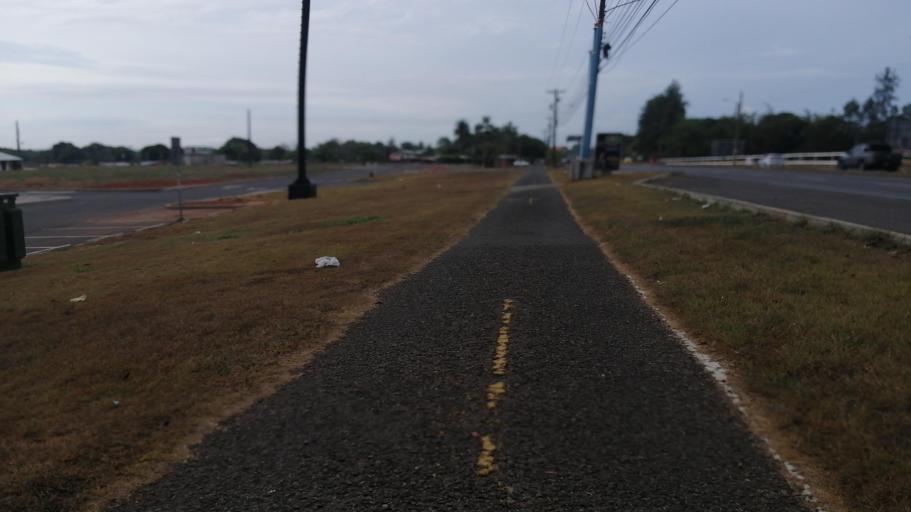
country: PA
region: Chiriqui
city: David
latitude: 8.4069
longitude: -82.4301
